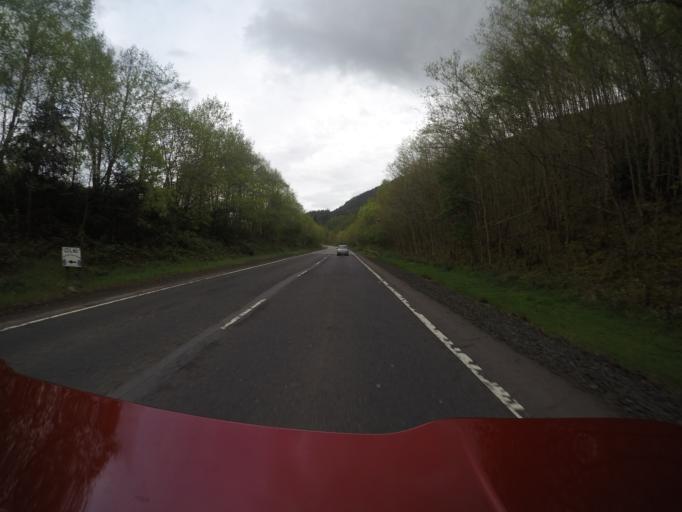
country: GB
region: Scotland
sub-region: Argyll and Bute
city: Helensburgh
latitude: 56.1222
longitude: -4.6519
